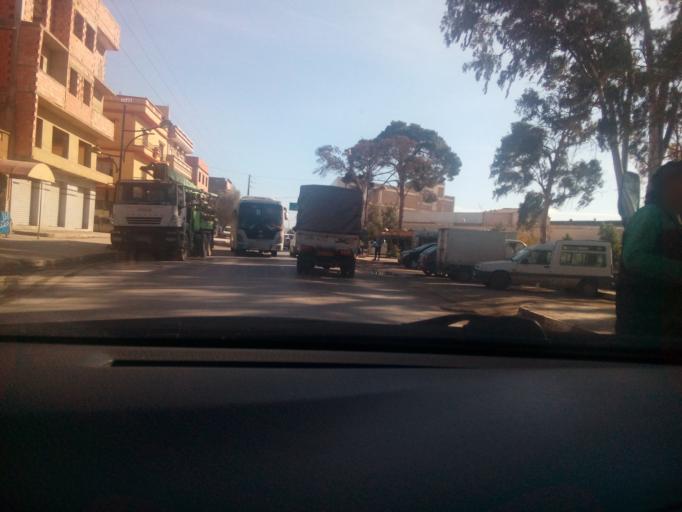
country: DZ
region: Oran
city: Sidi ech Chahmi
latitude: 35.6700
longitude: -0.5687
